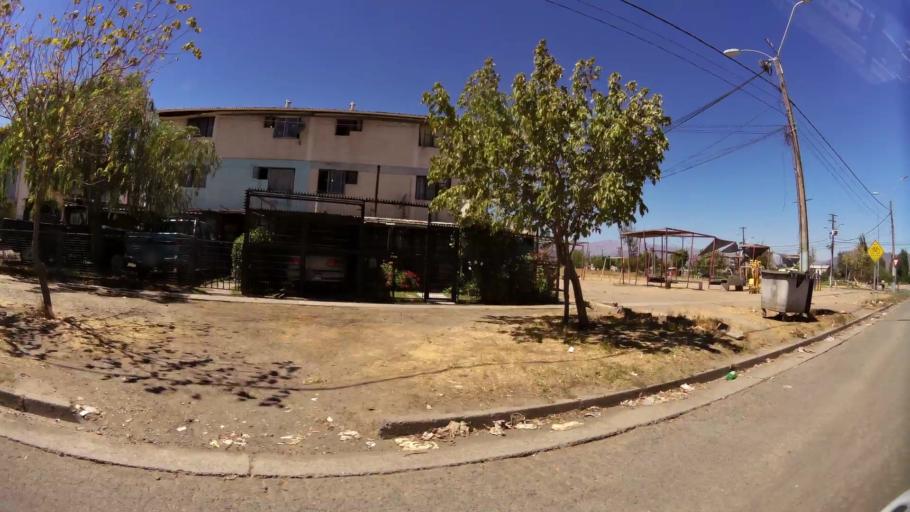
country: CL
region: O'Higgins
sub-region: Provincia de Cachapoal
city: Rancagua
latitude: -34.1528
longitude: -70.7168
